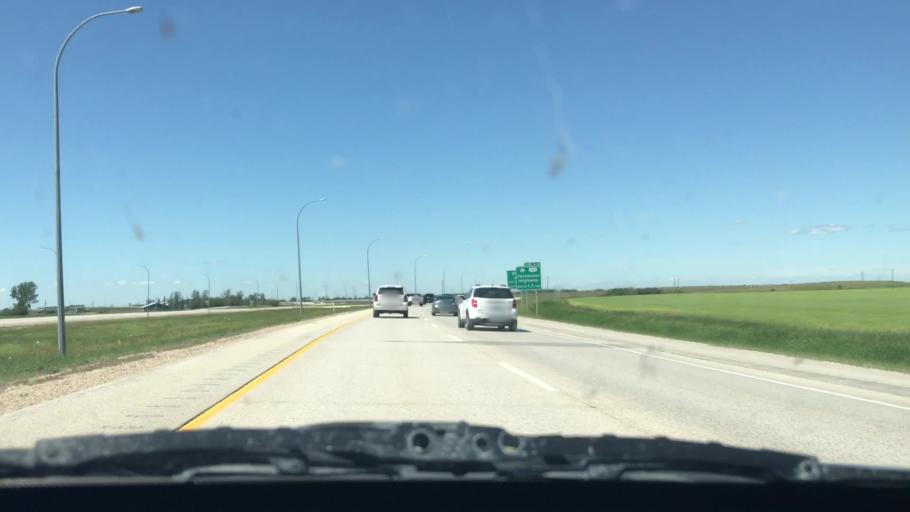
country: CA
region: Manitoba
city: Winnipeg
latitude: 49.8238
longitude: -96.9434
